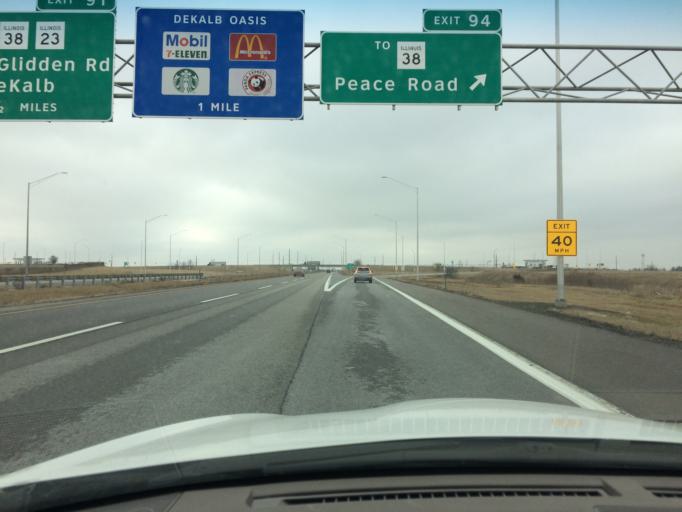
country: US
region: Illinois
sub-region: DeKalb County
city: Cortland
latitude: 41.9006
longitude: -88.7166
